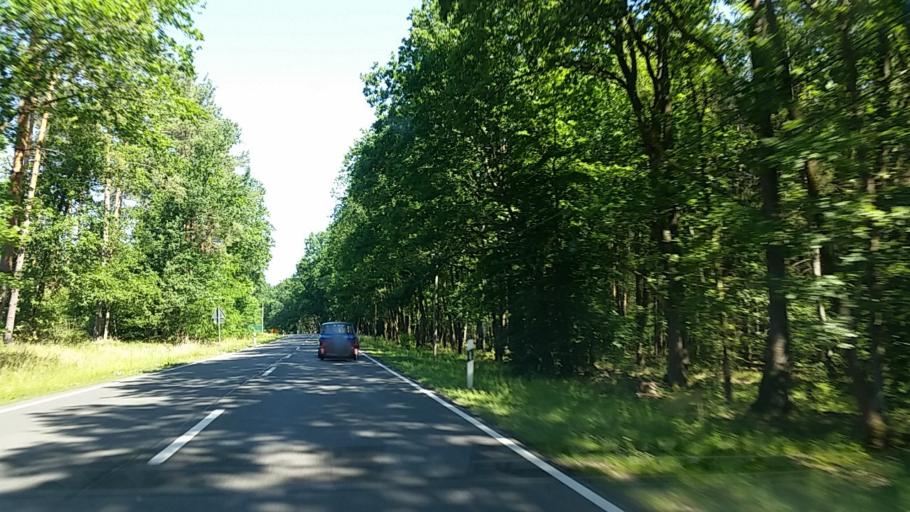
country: DE
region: Saxony-Anhalt
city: Kemberg
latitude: 51.7196
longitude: 12.6173
